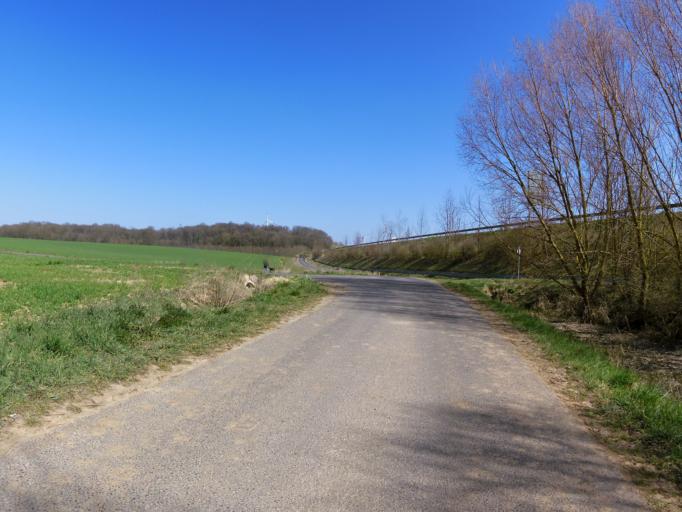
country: DE
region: Bavaria
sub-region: Regierungsbezirk Unterfranken
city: Biebelried
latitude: 49.7683
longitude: 10.0788
